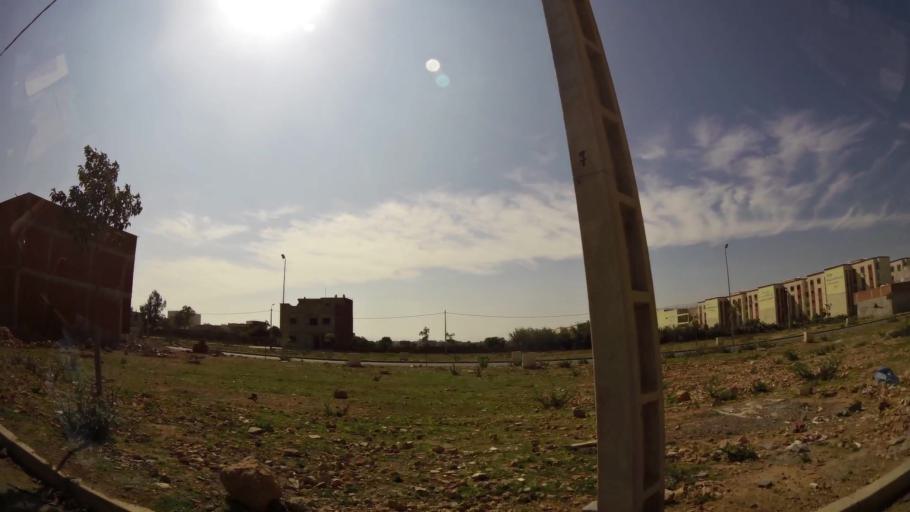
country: MA
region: Oriental
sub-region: Oujda-Angad
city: Oujda
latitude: 34.6968
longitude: -1.8729
